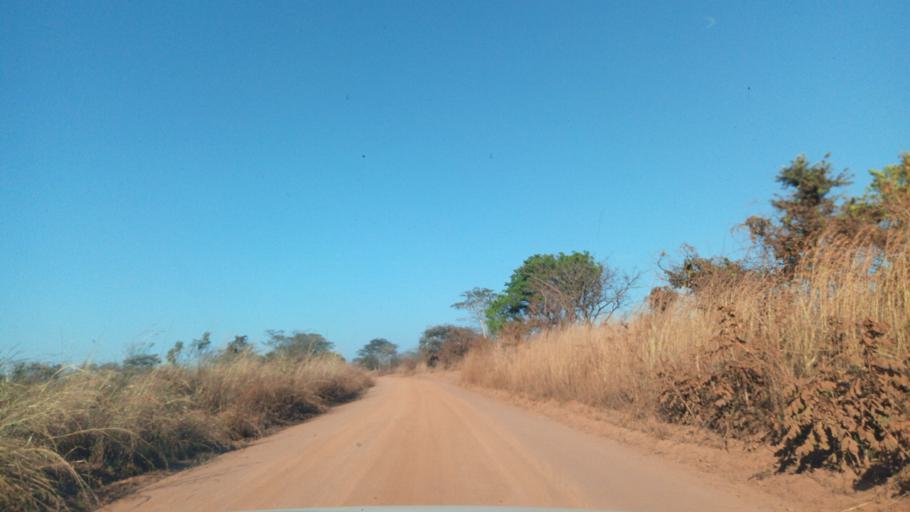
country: ZM
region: Luapula
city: Mwense
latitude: -10.5177
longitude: 28.4595
